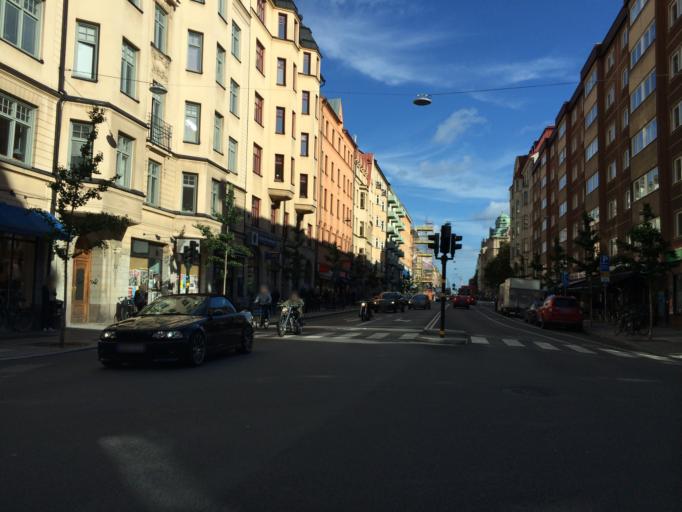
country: SE
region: Stockholm
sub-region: Stockholms Kommun
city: Stockholm
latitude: 59.3185
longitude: 18.0598
